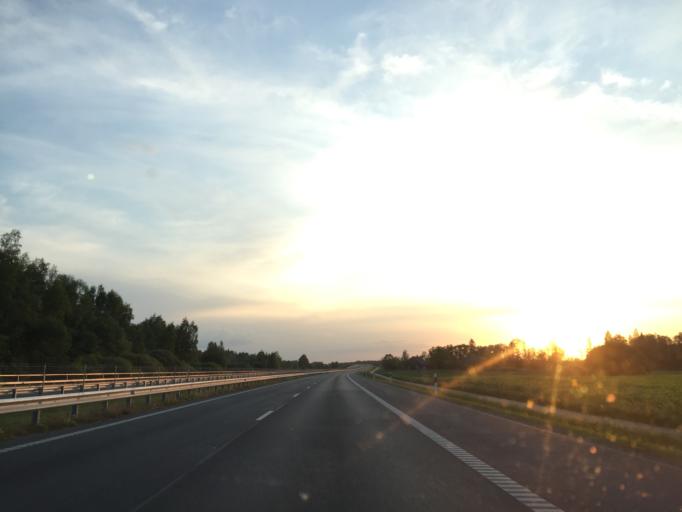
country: LT
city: Kursenai
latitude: 55.9853
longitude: 23.0925
